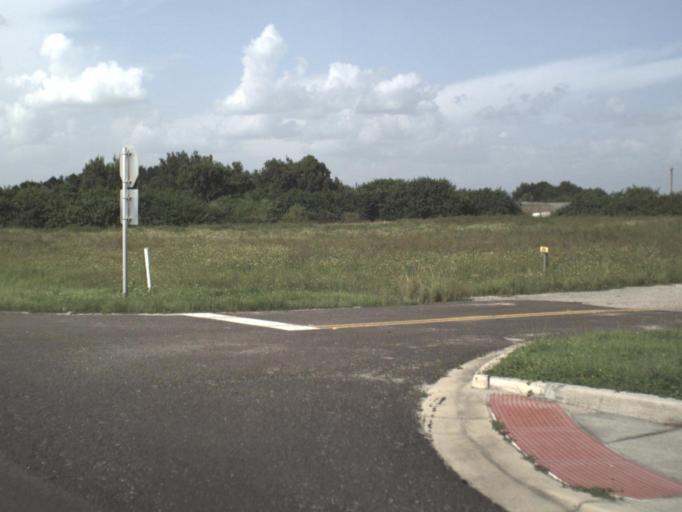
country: US
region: Florida
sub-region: Polk County
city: Lake Hamilton
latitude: 28.0340
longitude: -81.6359
